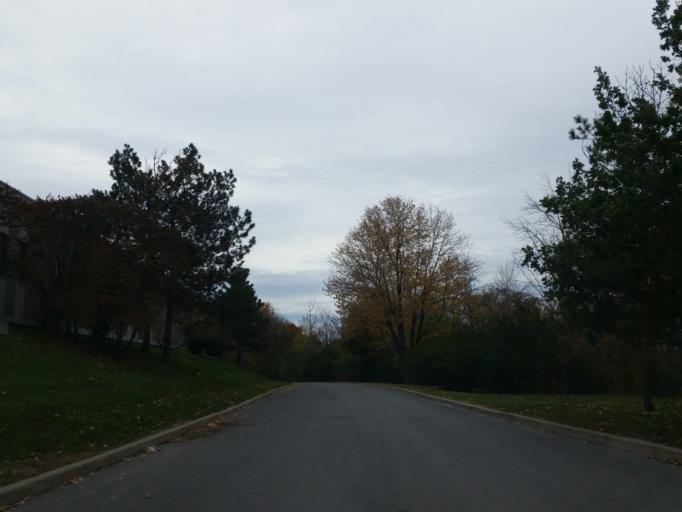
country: CA
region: Ontario
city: Bells Corners
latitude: 45.3753
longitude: -75.7922
